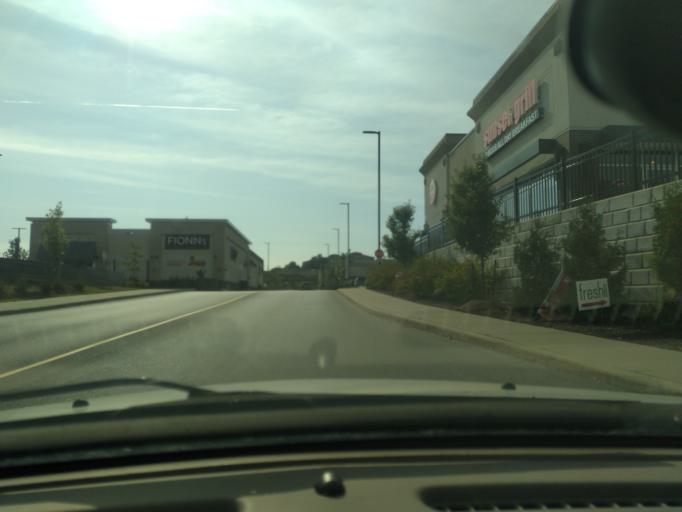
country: CA
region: Ontario
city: Barrie
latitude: 44.4154
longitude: -79.6788
